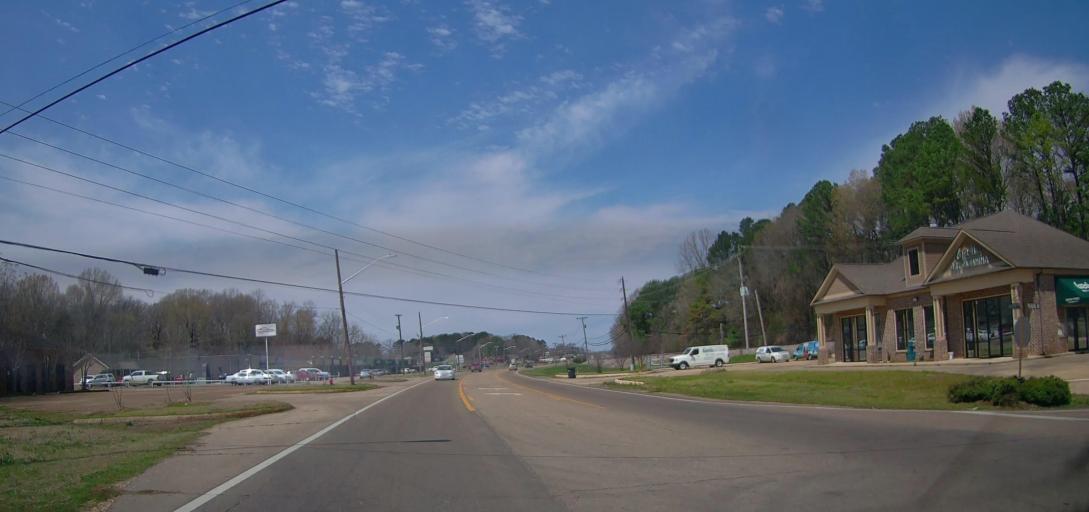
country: US
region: Mississippi
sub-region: Union County
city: New Albany
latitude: 34.4971
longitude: -89.0213
